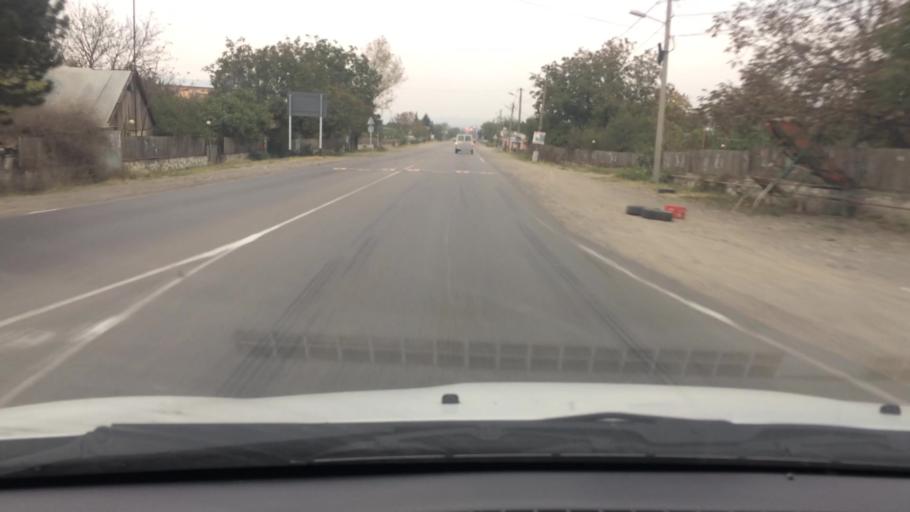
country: GE
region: Kvemo Kartli
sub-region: Marneuli
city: Marneuli
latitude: 41.5792
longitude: 44.7744
